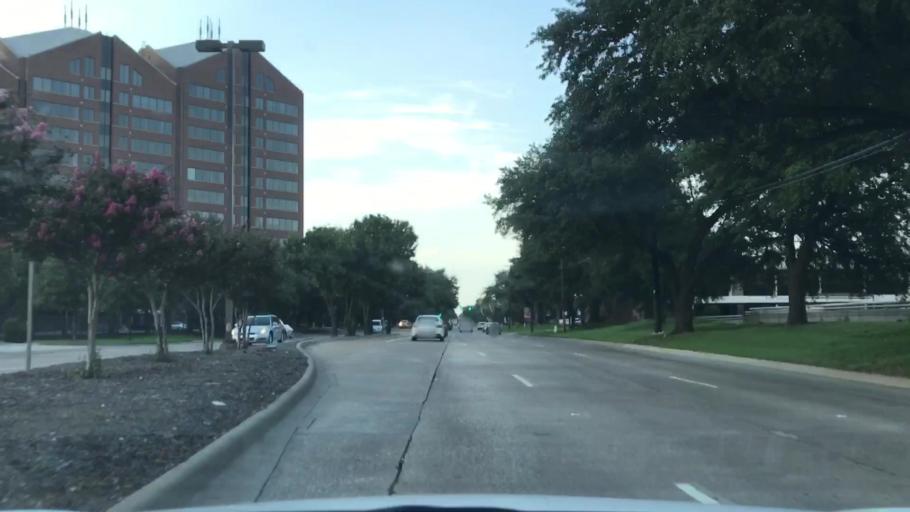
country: US
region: Texas
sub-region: Dallas County
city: Addison
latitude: 32.9411
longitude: -96.8389
